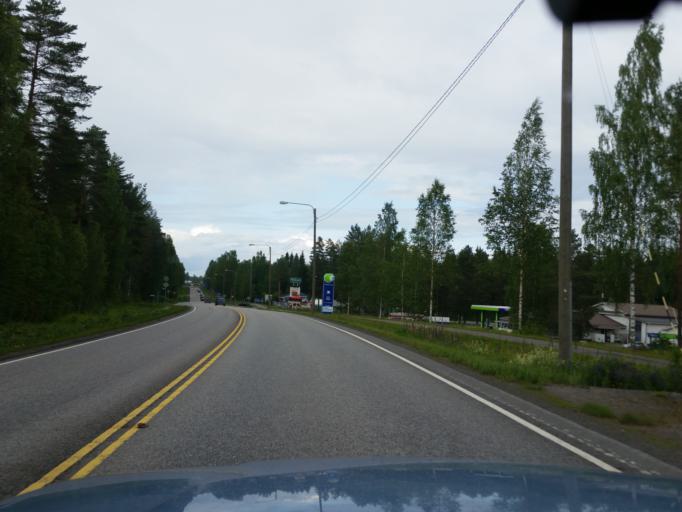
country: FI
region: Southern Savonia
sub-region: Pieksaemaeki
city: Juva
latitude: 61.8877
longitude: 27.7948
